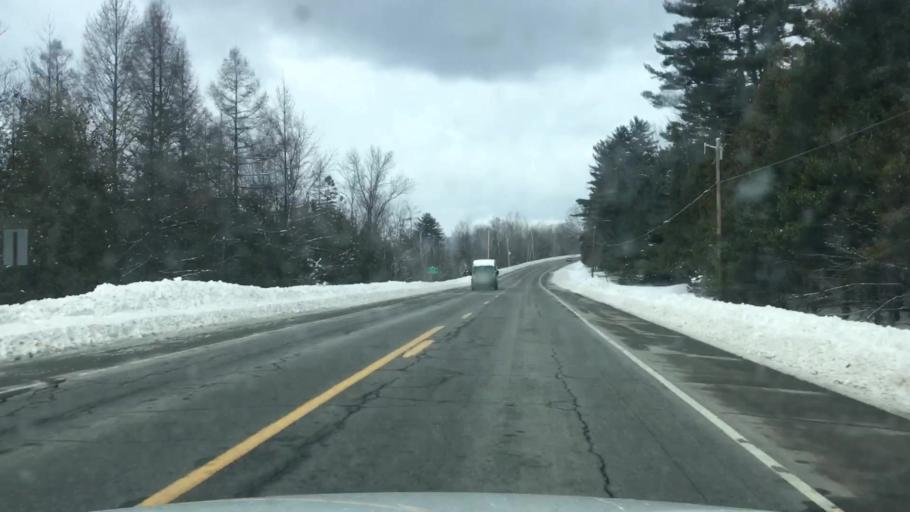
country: US
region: Maine
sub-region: Somerset County
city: Cornville
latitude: 44.8090
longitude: -69.7055
